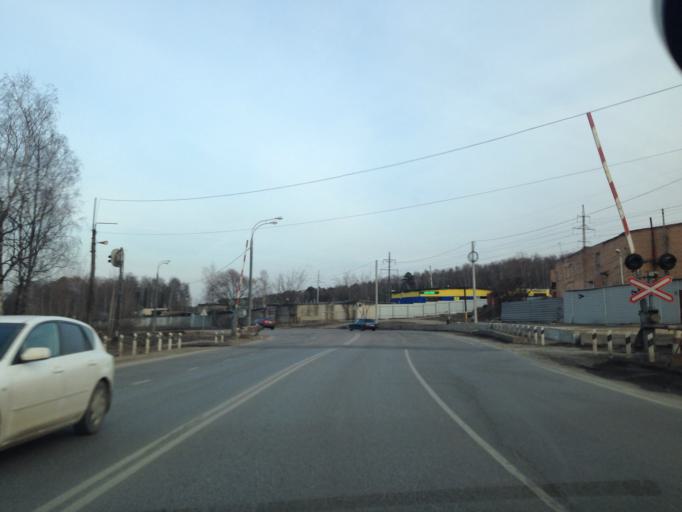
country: RU
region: Moskovskaya
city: Saltykovka
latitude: 55.8050
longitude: 37.9111
